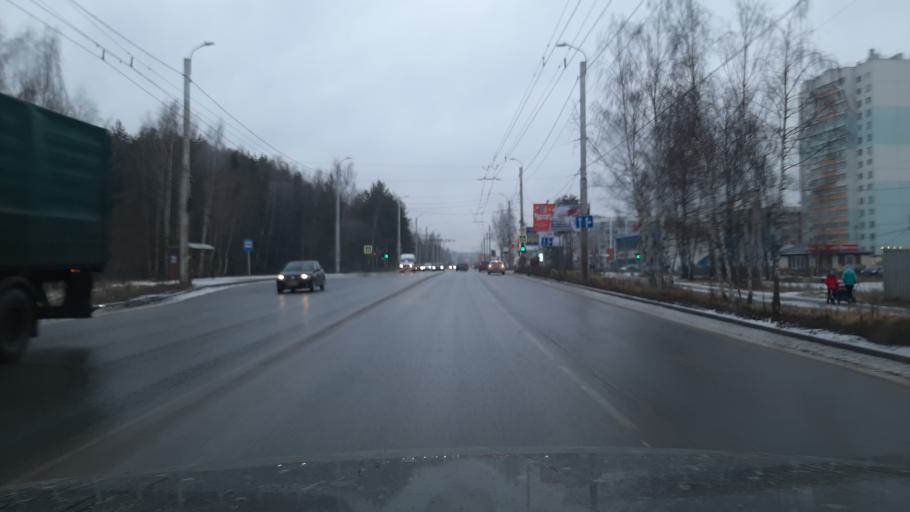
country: RU
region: Ivanovo
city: Kokhma
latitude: 56.9511
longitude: 41.0468
